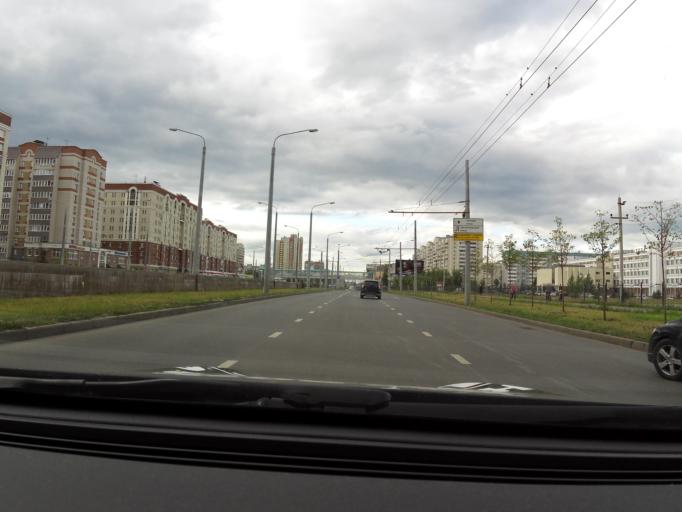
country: RU
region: Tatarstan
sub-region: Gorod Kazan'
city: Kazan
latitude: 55.8205
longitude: 49.1341
